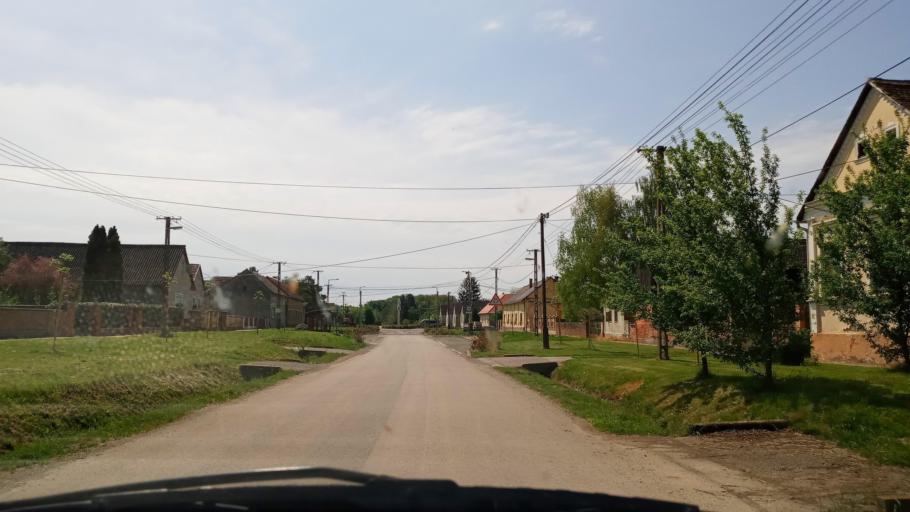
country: HR
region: Osjecko-Baranjska
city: Beli Manastir
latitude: 45.8632
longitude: 18.5859
